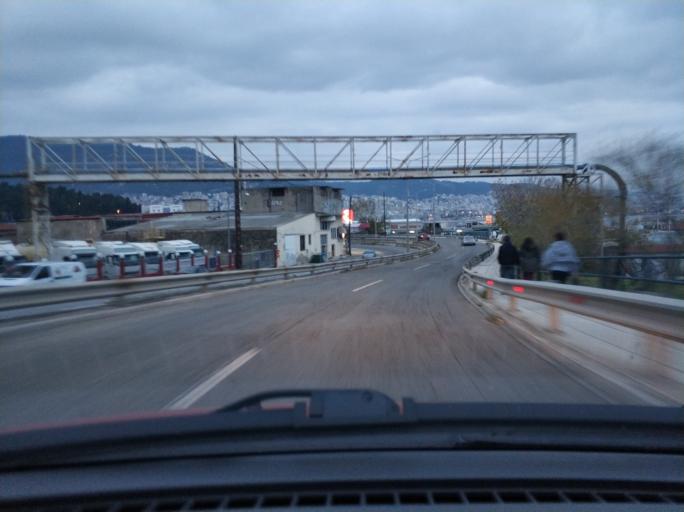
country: GR
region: East Macedonia and Thrace
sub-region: Nomos Kavalas
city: Kavala
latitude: 40.9257
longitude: 24.3904
